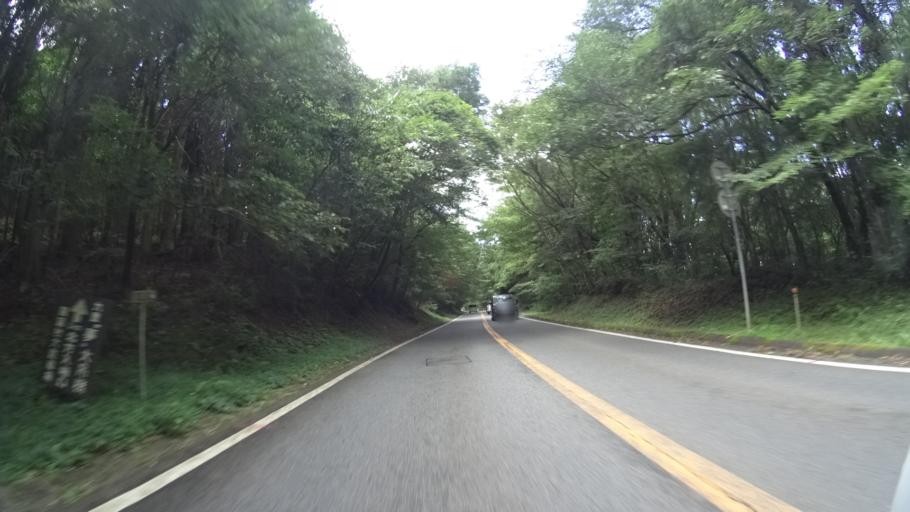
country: JP
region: Oita
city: Tsukawaki
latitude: 33.1971
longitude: 131.2585
